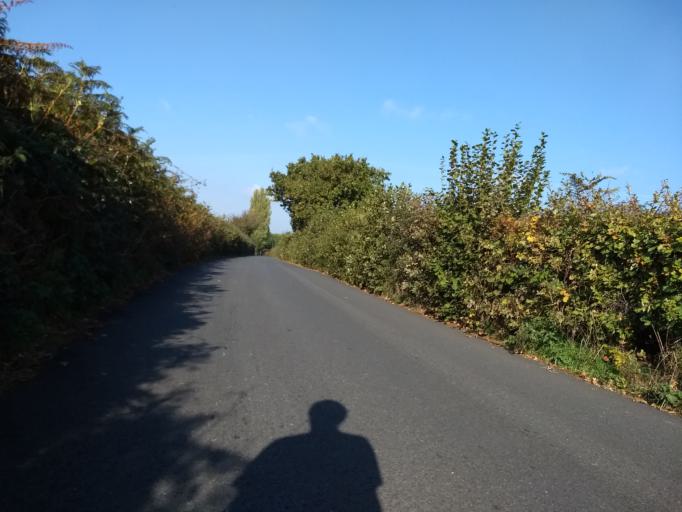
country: GB
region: England
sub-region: Isle of Wight
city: Newchurch
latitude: 50.7220
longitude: -1.2188
